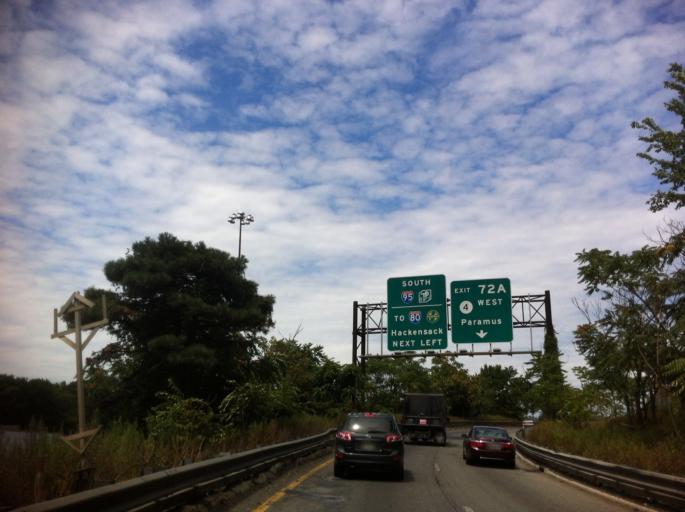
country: US
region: New Jersey
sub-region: Bergen County
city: Fort Lee
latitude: 40.8589
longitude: -73.9748
